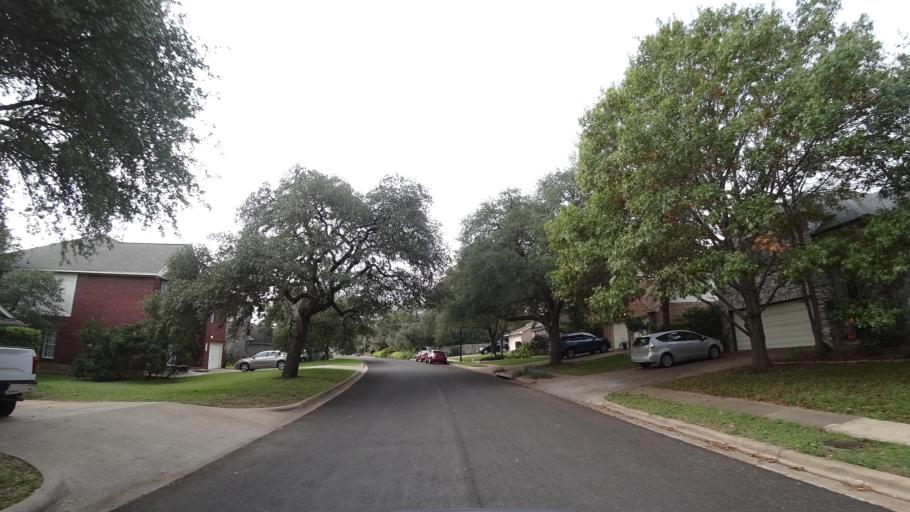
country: US
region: Texas
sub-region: Travis County
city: Shady Hollow
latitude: 30.1915
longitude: -97.8884
